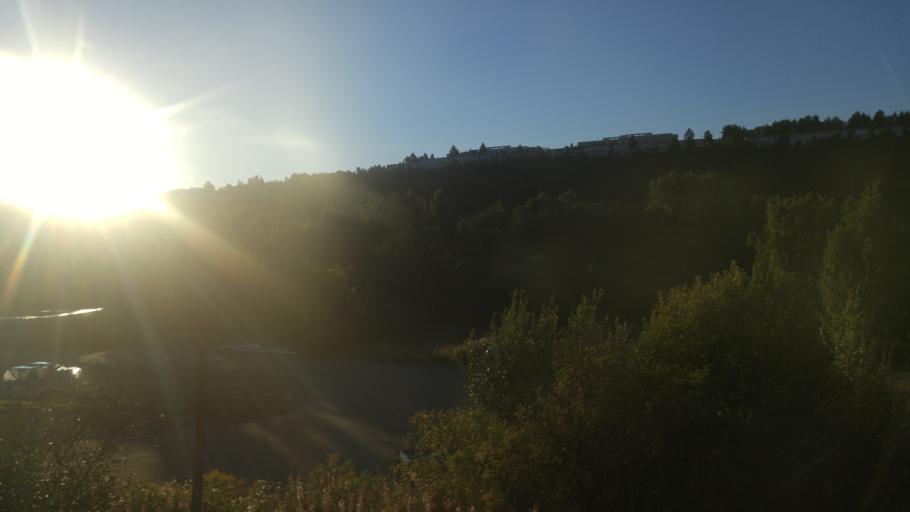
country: NO
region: Oslo
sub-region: Oslo
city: Oslo
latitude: 59.9201
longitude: 10.8316
